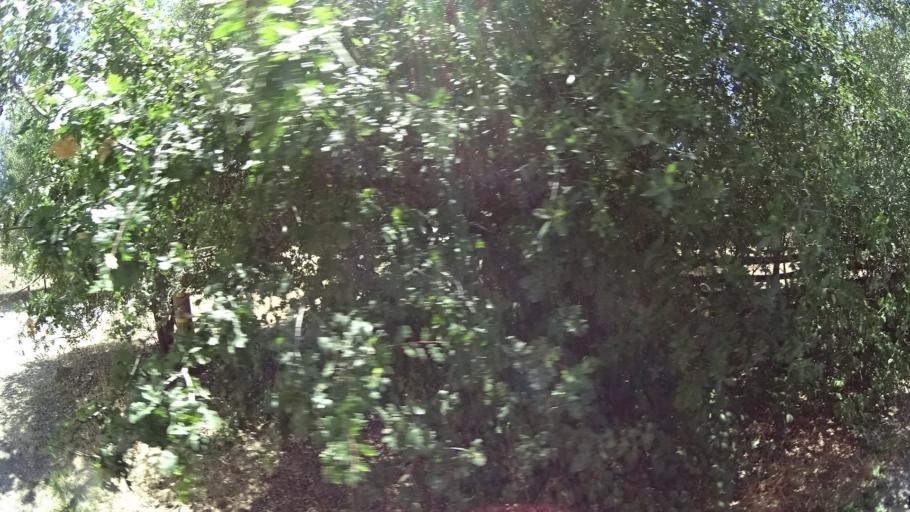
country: US
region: California
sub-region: Calaveras County
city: Forest Meadows
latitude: 38.2104
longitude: -120.4663
